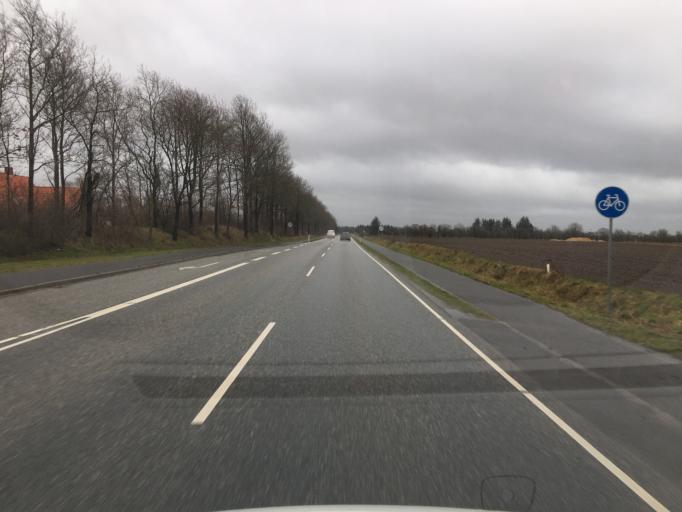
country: DK
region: South Denmark
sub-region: Aabenraa Kommune
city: Tinglev
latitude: 54.9276
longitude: 9.2421
